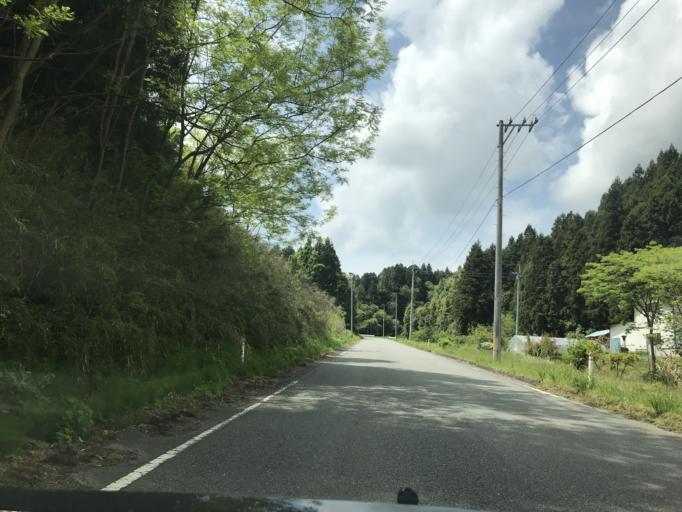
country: JP
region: Miyagi
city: Furukawa
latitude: 38.7377
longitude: 140.9297
